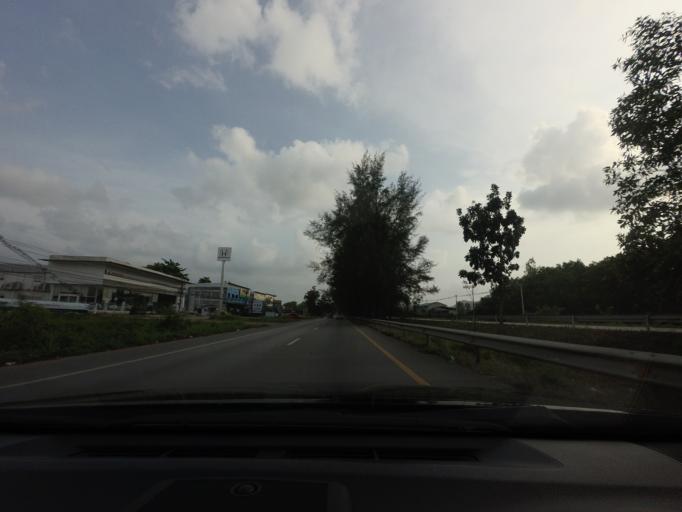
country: TH
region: Chumphon
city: Lang Suan
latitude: 9.9317
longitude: 99.0601
